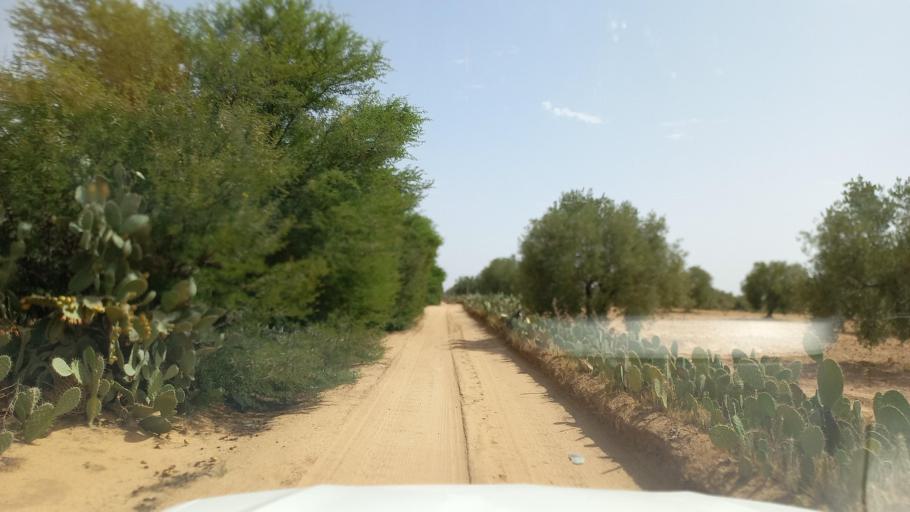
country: TN
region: Al Qasrayn
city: Kasserine
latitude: 35.2576
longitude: 9.0537
